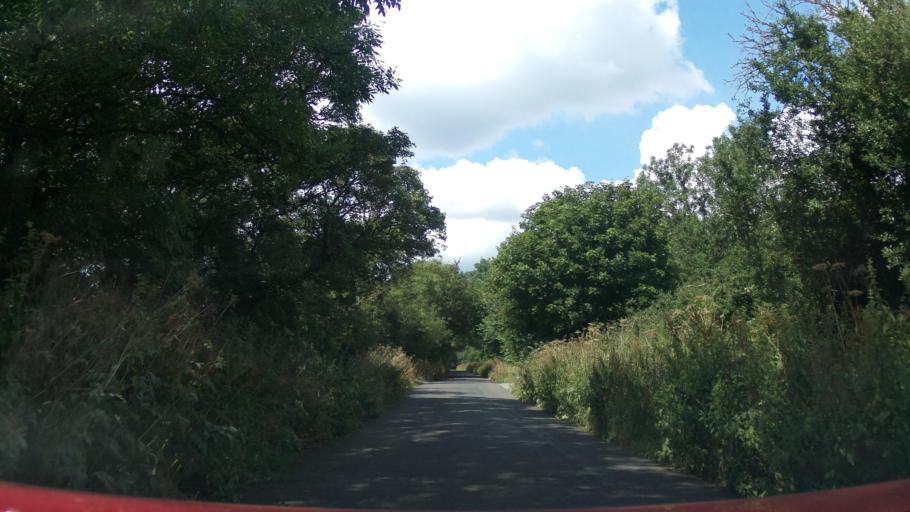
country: GB
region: England
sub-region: Wiltshire
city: Hankerton
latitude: 51.6239
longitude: -2.0591
